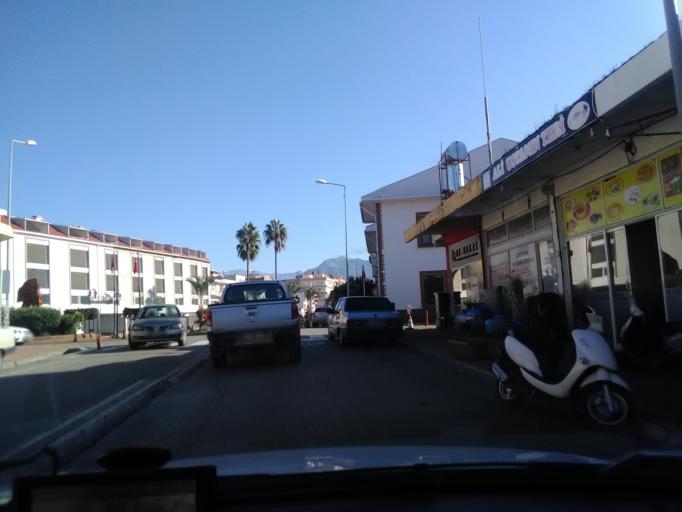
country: TR
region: Antalya
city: Gazipasa
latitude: 36.2679
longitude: 32.3161
